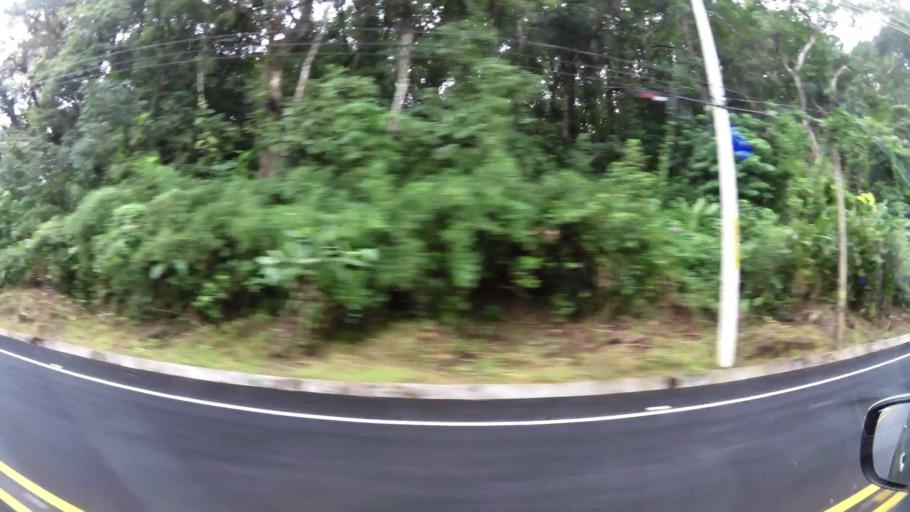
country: CR
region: Alajuela
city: Orotina
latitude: 9.9501
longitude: -84.5702
